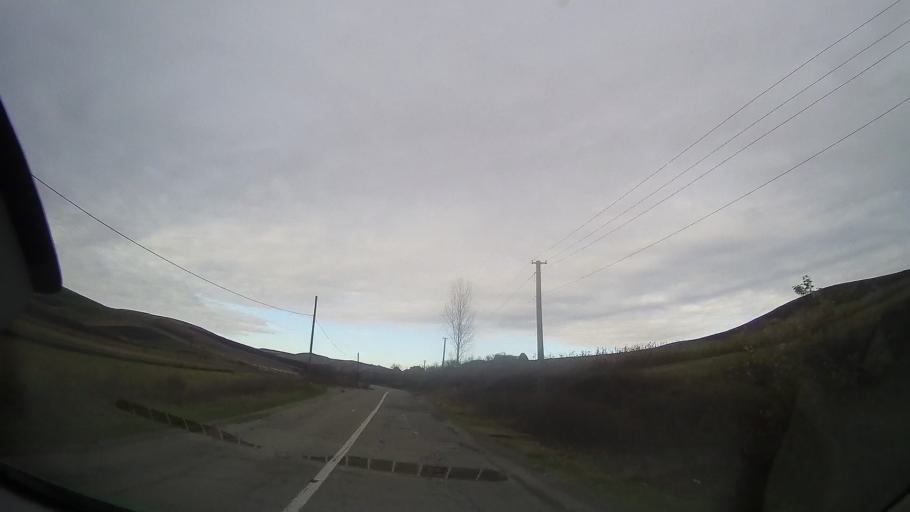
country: RO
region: Cluj
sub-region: Comuna Camarasu
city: Camarasu
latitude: 46.8058
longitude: 24.1459
